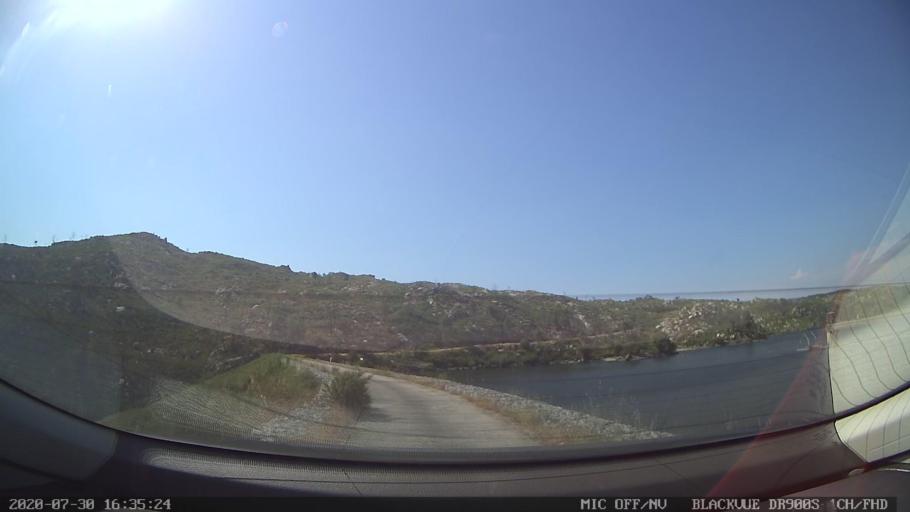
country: PT
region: Vila Real
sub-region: Sabrosa
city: Sabrosa
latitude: 41.3078
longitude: -7.4904
